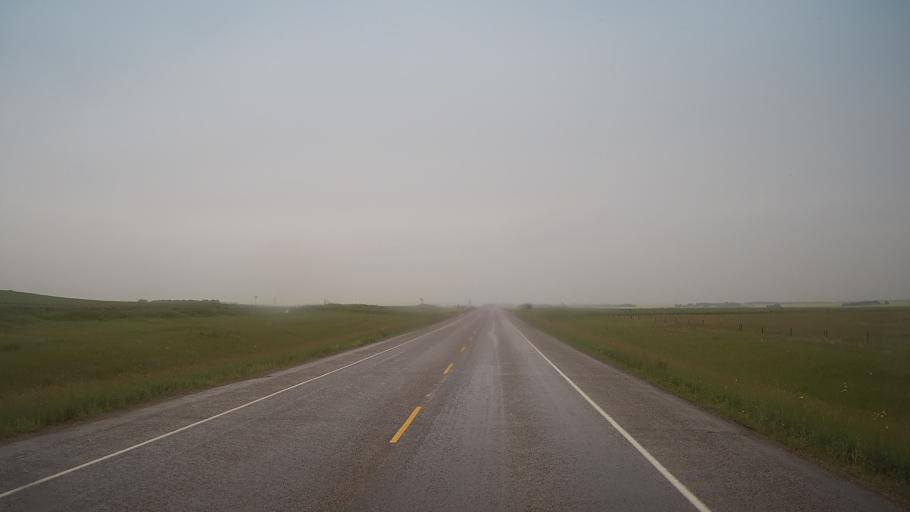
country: CA
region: Saskatchewan
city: Wilkie
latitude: 52.1873
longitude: -108.4048
